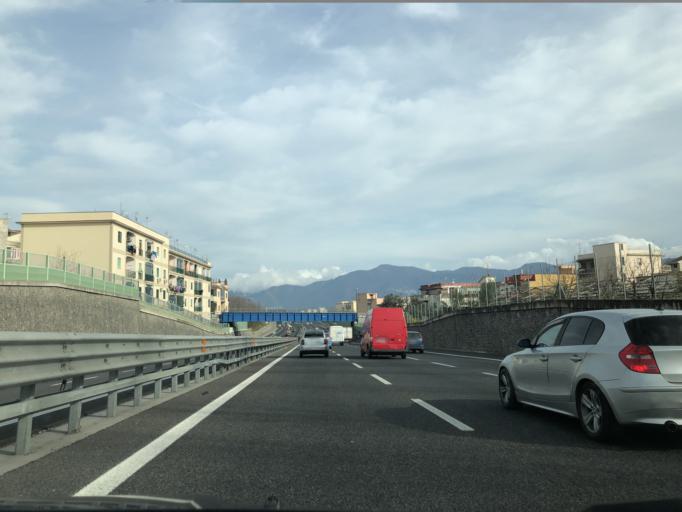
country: IT
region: Campania
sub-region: Provincia di Napoli
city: Trecase
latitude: 40.7635
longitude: 14.4384
